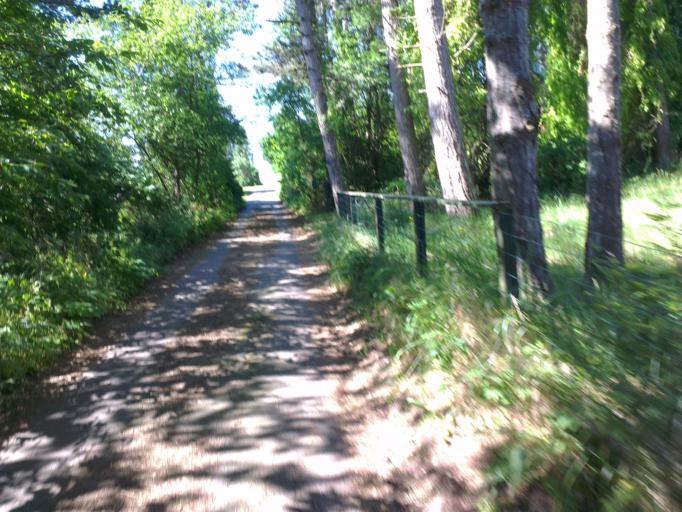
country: DK
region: Capital Region
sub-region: Halsnaes Kommune
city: Hundested
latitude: 55.9258
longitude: 11.9051
